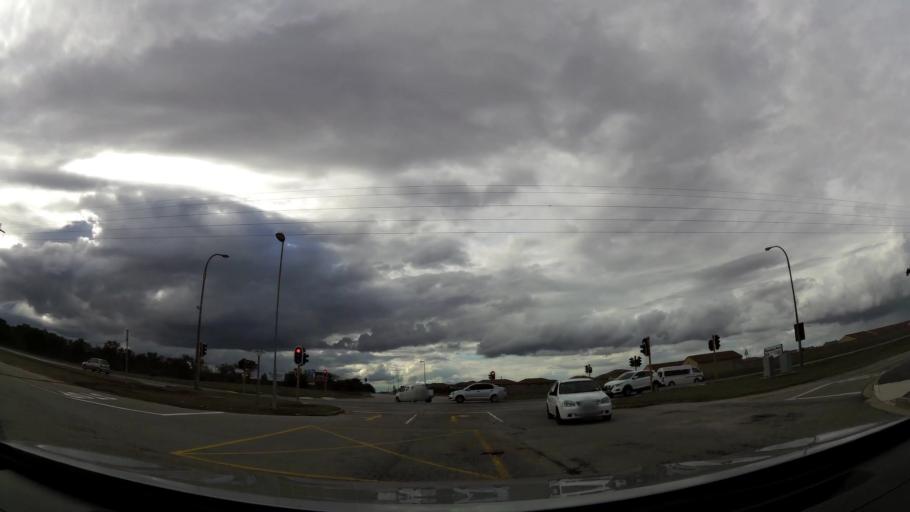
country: ZA
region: Eastern Cape
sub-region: Nelson Mandela Bay Metropolitan Municipality
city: Port Elizabeth
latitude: -33.9340
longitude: 25.4642
